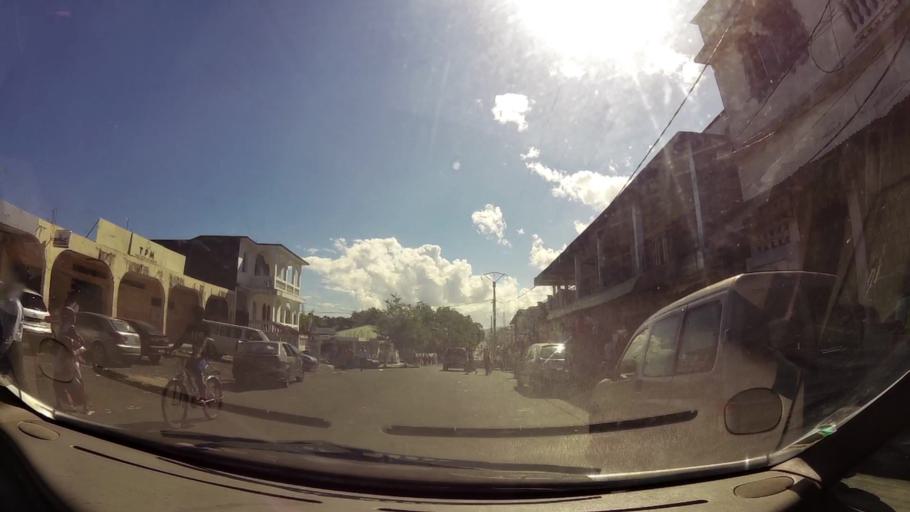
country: KM
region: Grande Comore
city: Moroni
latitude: -11.6966
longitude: 43.2548
